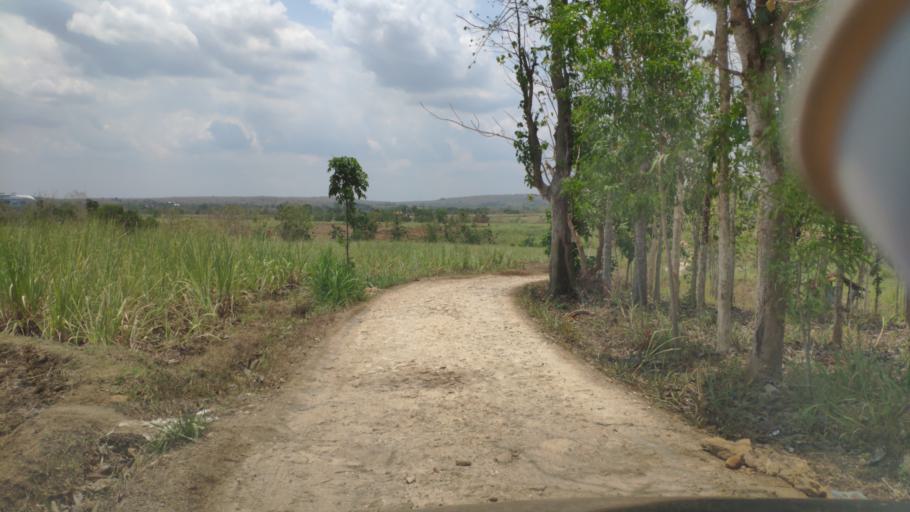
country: ID
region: Central Java
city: Ngapus
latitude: -6.9689
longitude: 111.2179
